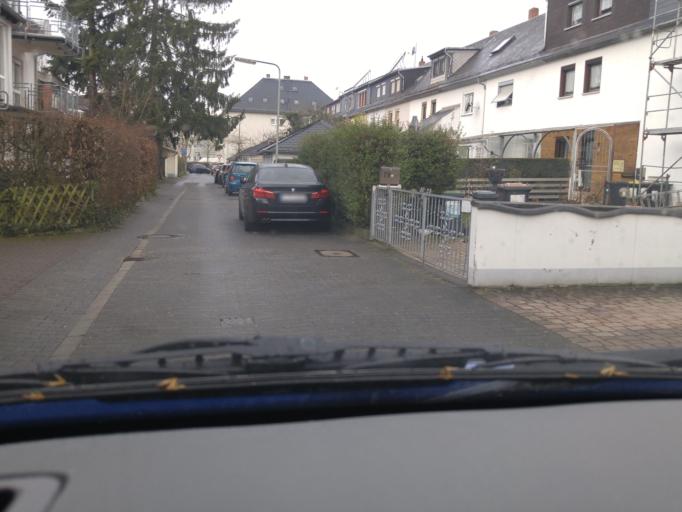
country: DE
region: Hesse
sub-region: Regierungsbezirk Darmstadt
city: Bad Vilbel
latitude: 50.1839
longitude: 8.6720
